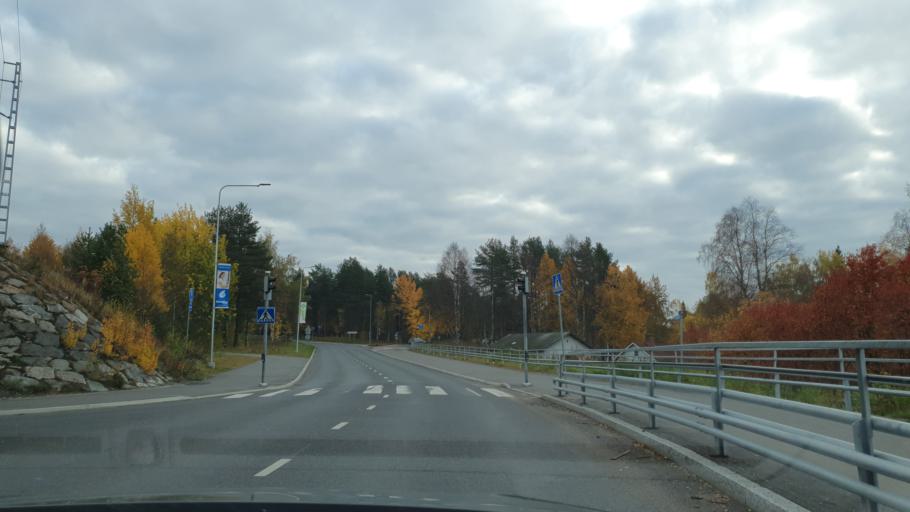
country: FI
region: Lapland
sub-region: Rovaniemi
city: Rovaniemi
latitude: 66.4963
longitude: 25.7406
